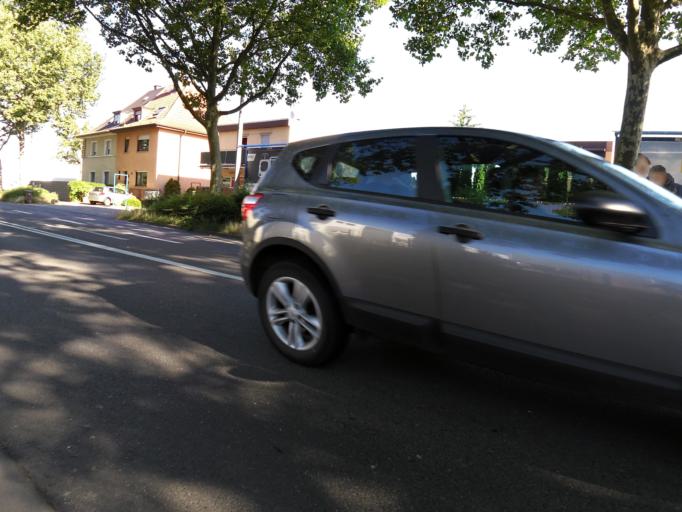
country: DE
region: Rheinland-Pfalz
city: Gartenstadt
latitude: 49.4875
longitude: 8.3951
